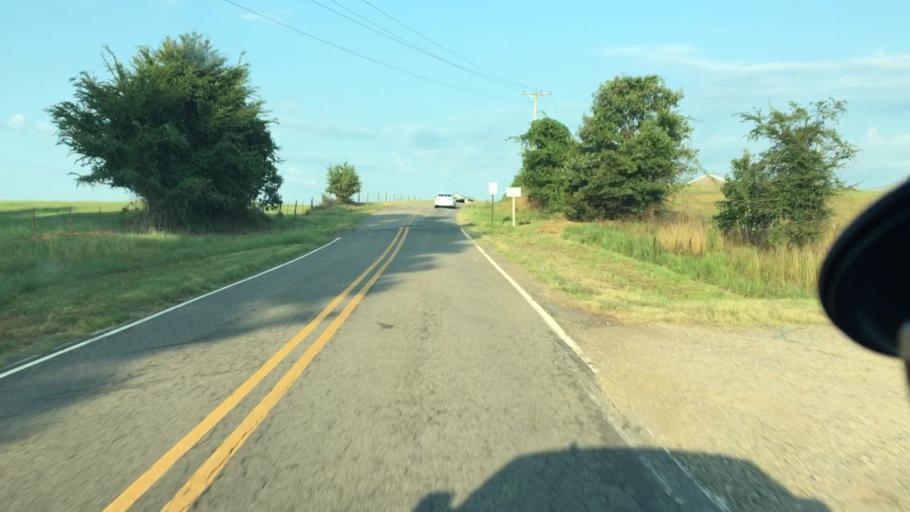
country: US
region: Arkansas
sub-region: Johnson County
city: Coal Hill
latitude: 35.3736
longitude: -93.5706
